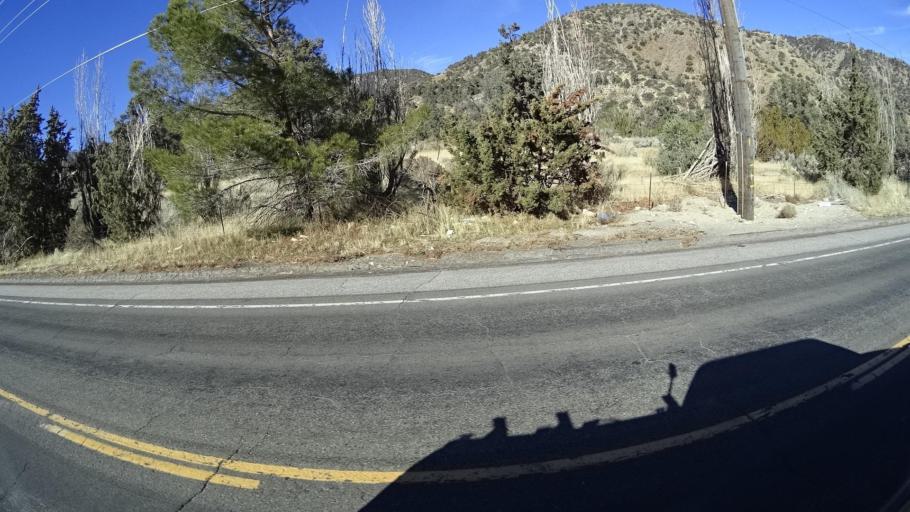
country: US
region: California
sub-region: Kern County
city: Frazier Park
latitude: 34.8200
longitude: -118.9298
